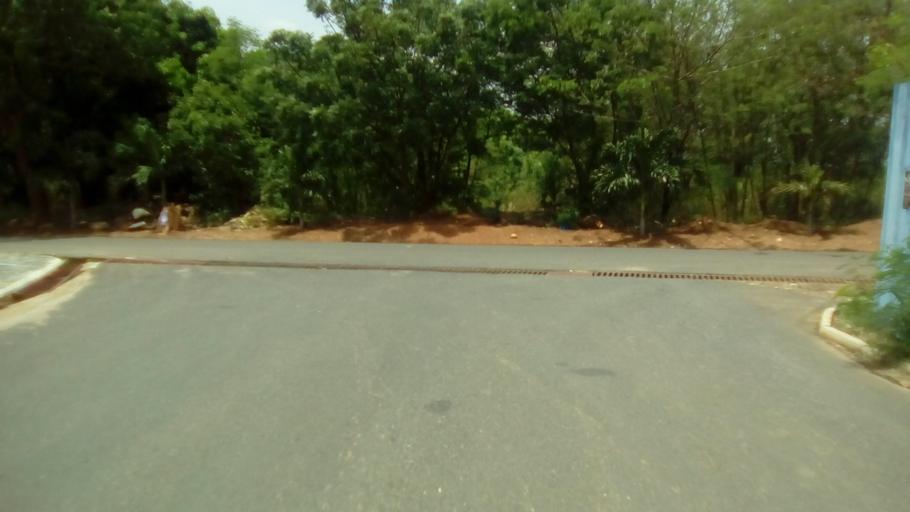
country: GH
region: Greater Accra
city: Medina Estates
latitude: 5.6565
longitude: -0.1900
